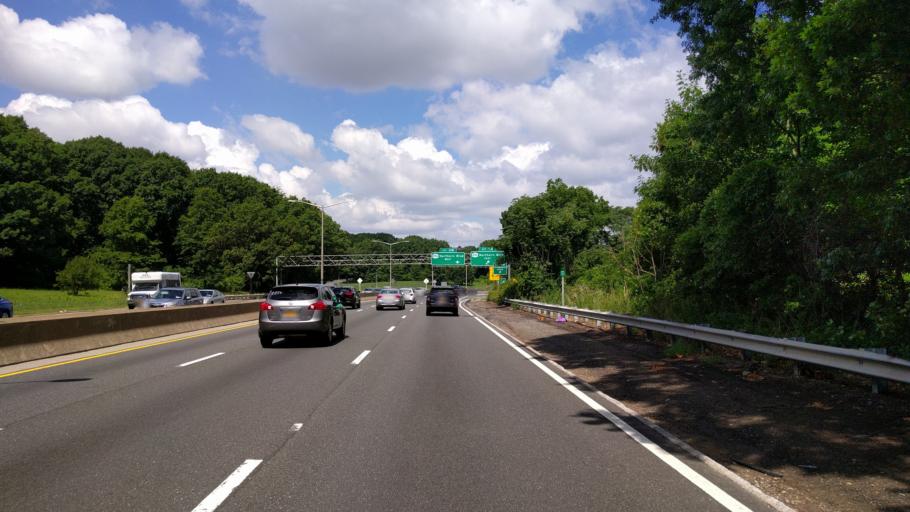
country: US
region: New York
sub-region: Nassau County
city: East Atlantic Beach
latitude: 40.7604
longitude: -73.7530
